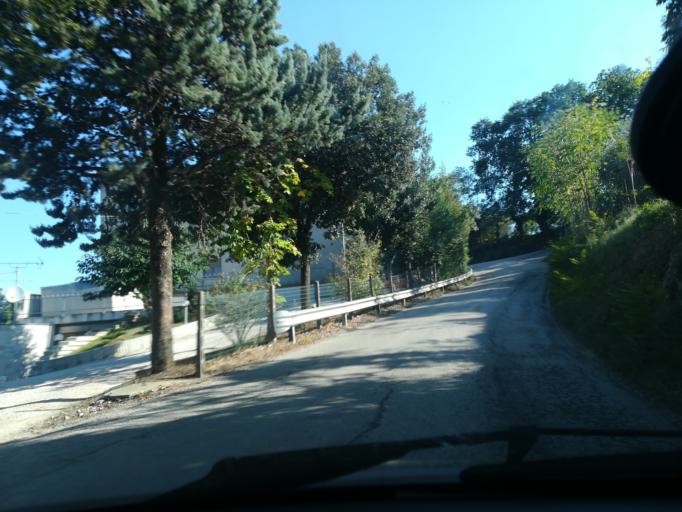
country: IT
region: The Marches
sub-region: Provincia di Macerata
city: Macerata
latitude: 43.3066
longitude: 13.4773
